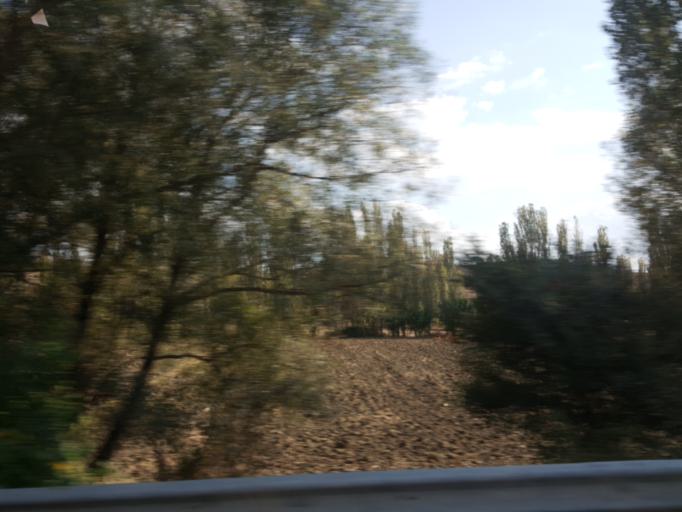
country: TR
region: Corum
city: Sungurlu
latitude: 40.1851
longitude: 34.4934
